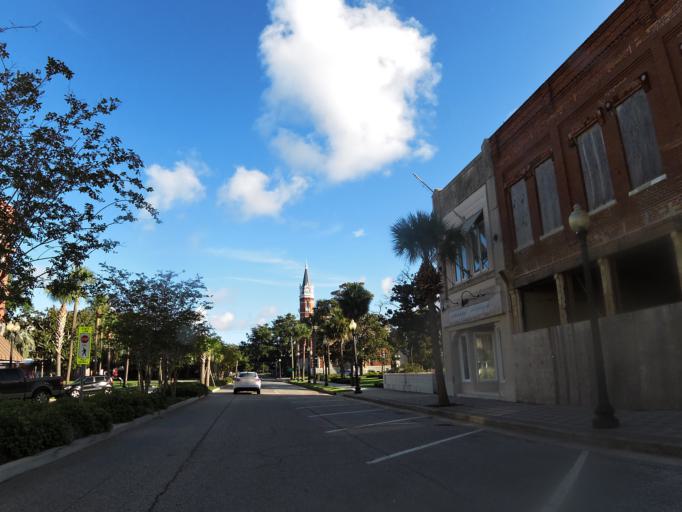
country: US
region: Georgia
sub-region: Glynn County
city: Brunswick
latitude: 31.1473
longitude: -81.4947
